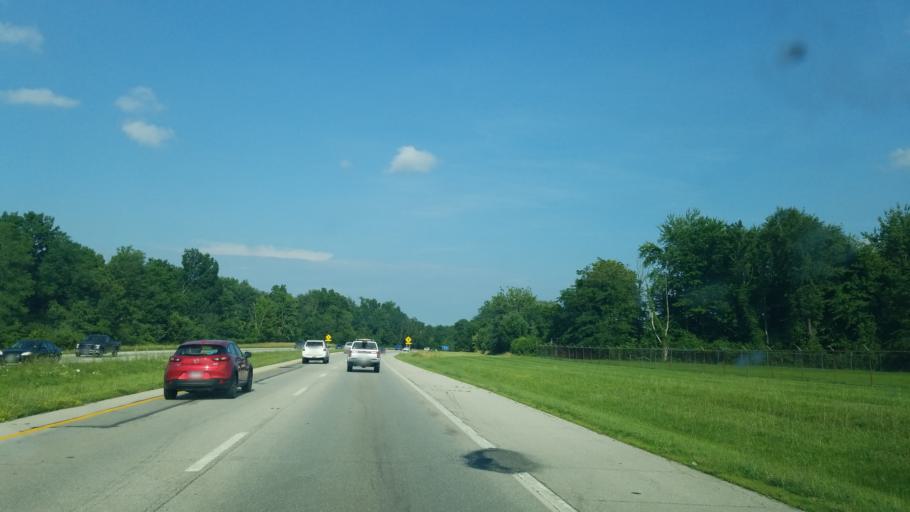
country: US
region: Ohio
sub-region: Clermont County
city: Batavia
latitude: 39.0884
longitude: -84.2105
